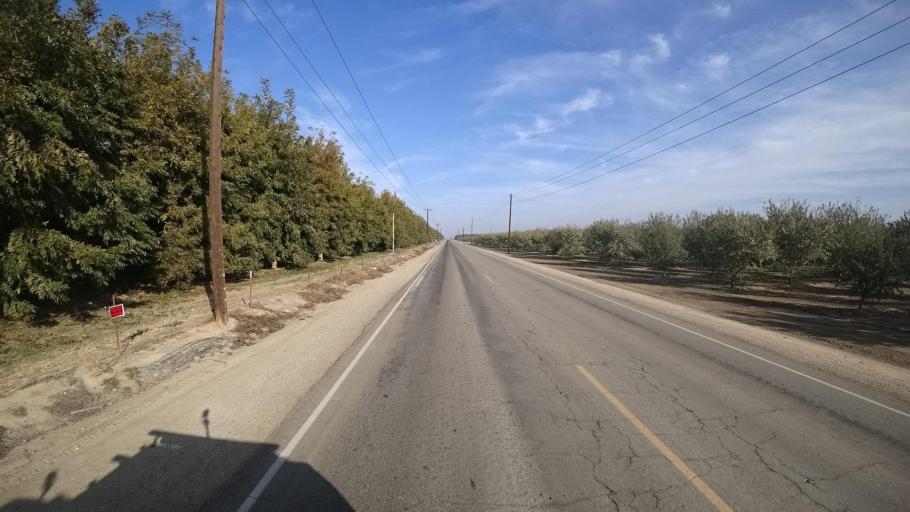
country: US
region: California
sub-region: Kern County
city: McFarland
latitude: 35.6288
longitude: -119.2043
